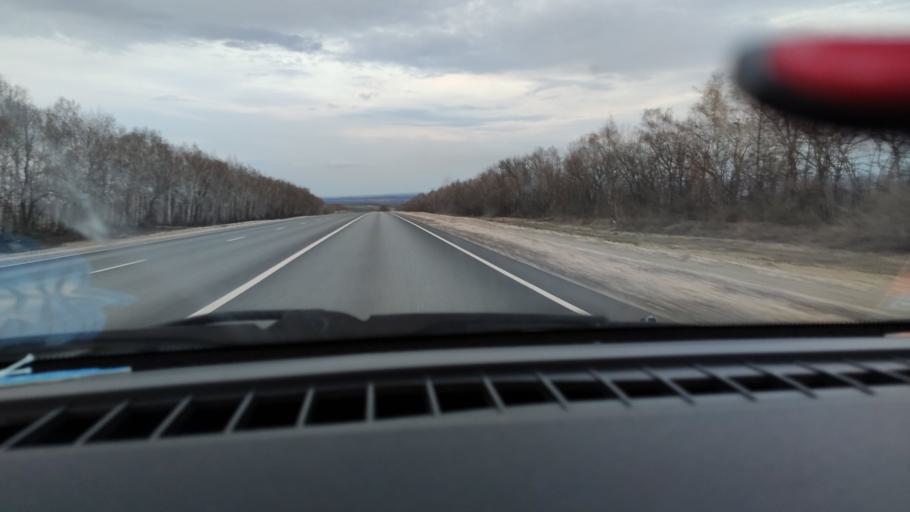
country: RU
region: Saratov
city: Sinodskoye
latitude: 51.9028
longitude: 46.5462
